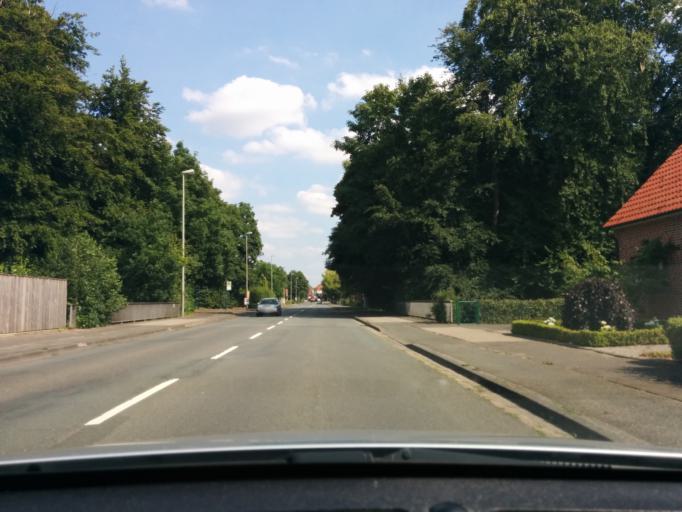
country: DE
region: North Rhine-Westphalia
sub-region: Regierungsbezirk Munster
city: Ochtrup
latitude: 52.1993
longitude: 7.2306
